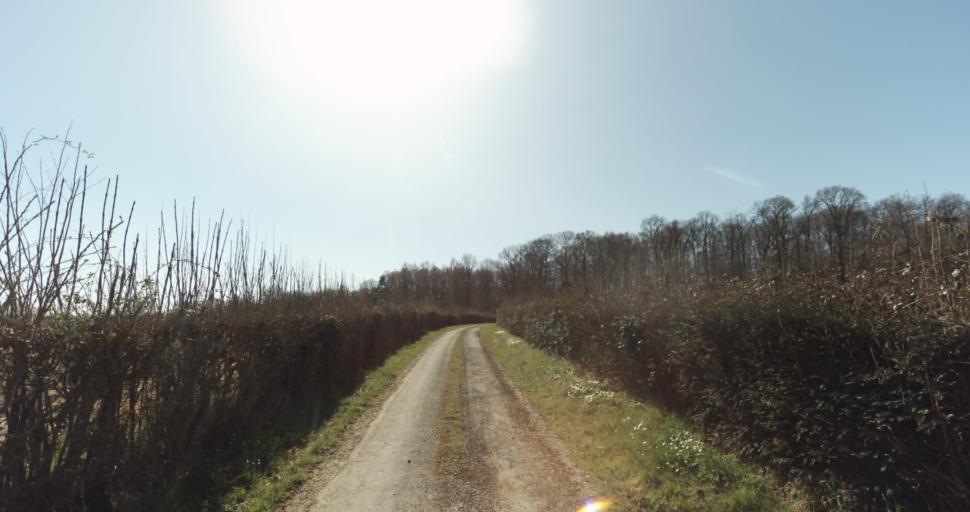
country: FR
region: Lower Normandy
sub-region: Departement du Calvados
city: Livarot
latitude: 48.9831
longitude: 0.0693
